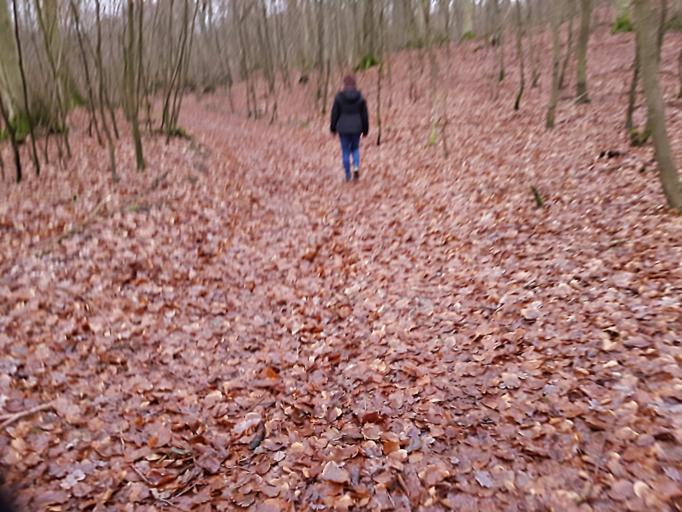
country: DE
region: Mecklenburg-Vorpommern
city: Ostseebad Binz
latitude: 54.3956
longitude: 13.6385
